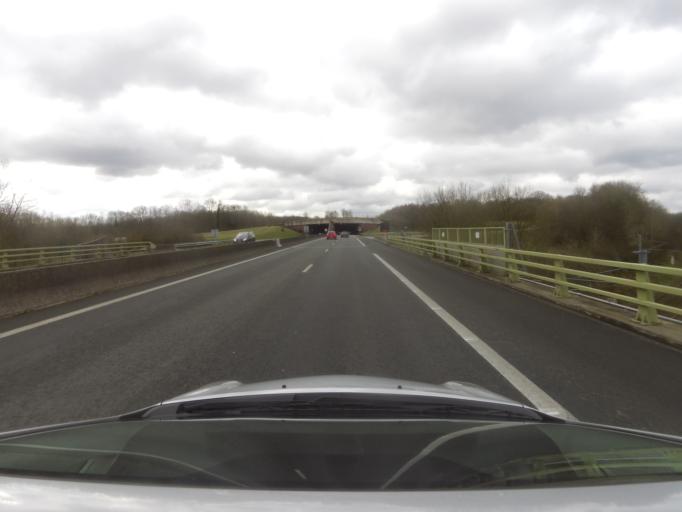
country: FR
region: Nord-Pas-de-Calais
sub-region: Departement du Pas-de-Calais
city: Nesles
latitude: 50.6455
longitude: 1.6656
